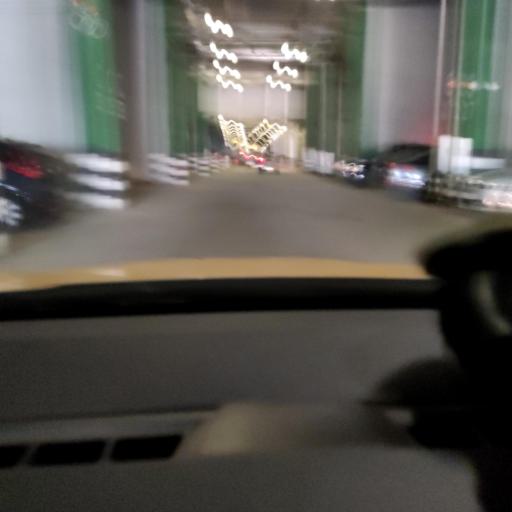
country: RU
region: Moscow
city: Leonovo
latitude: 55.8455
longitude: 37.6591
